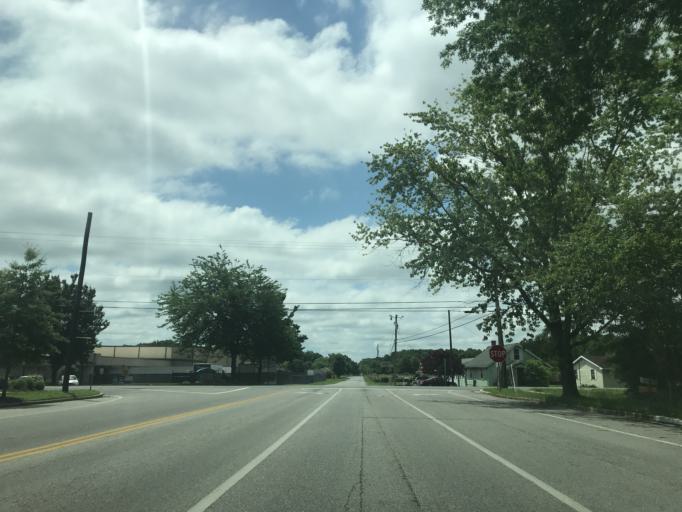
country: US
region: Maryland
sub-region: Caroline County
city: Ridgely
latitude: 38.9427
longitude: -75.8813
